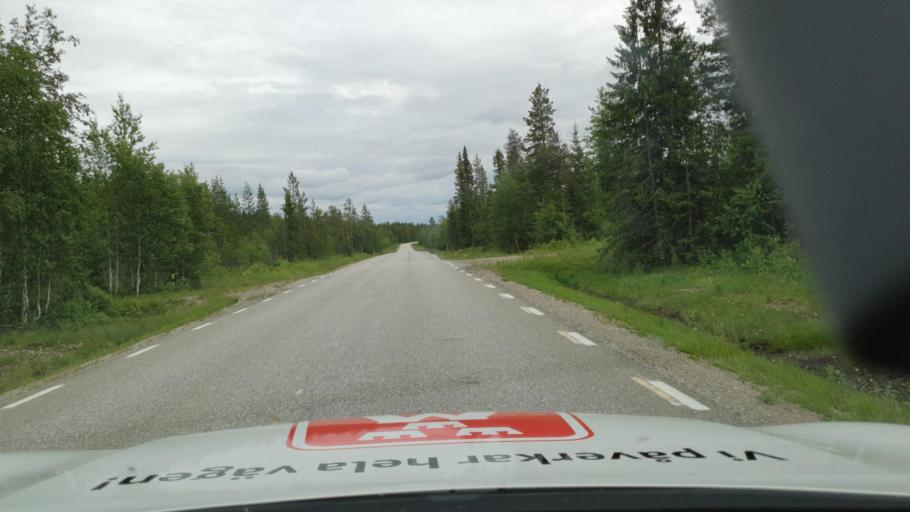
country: SE
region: Vaesterbotten
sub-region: Lycksele Kommun
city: Soderfors
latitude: 64.3260
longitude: 18.1502
